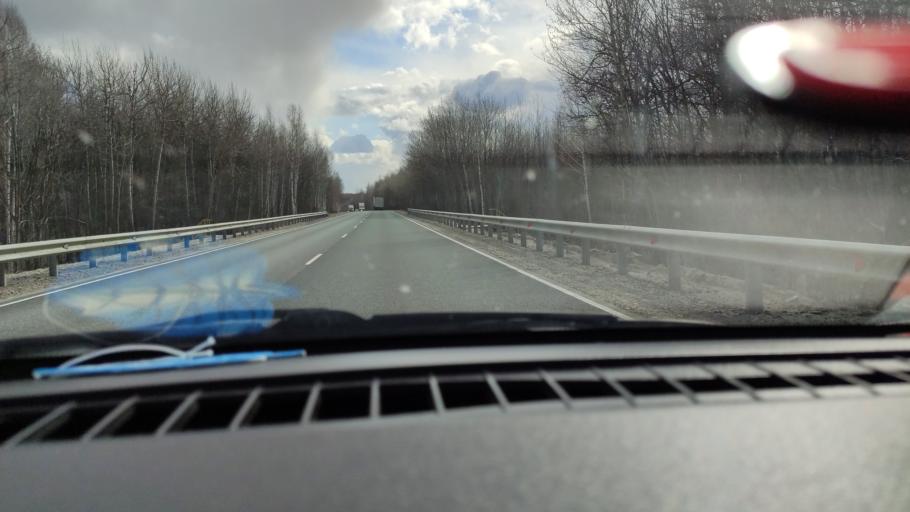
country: RU
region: Saratov
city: Khvalynsk
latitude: 52.4454
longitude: 48.0099
